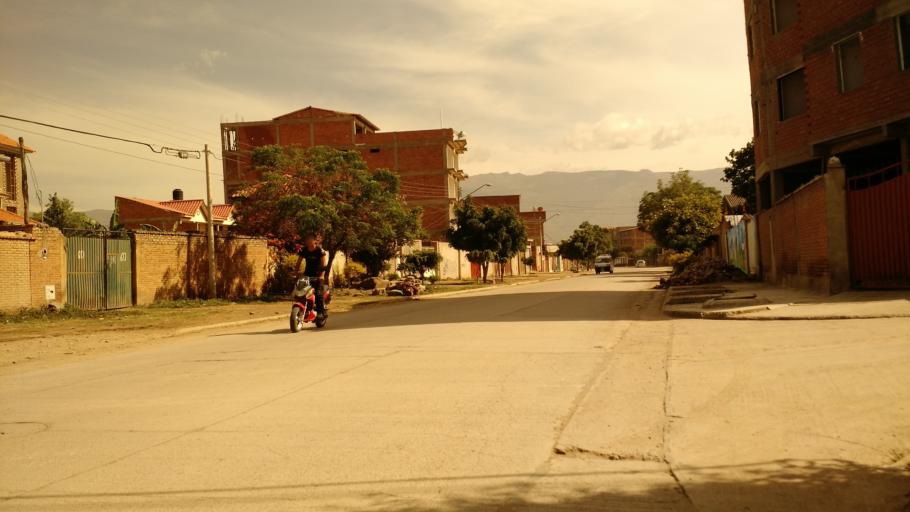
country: BO
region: Cochabamba
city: Cochabamba
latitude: -17.4326
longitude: -66.1595
